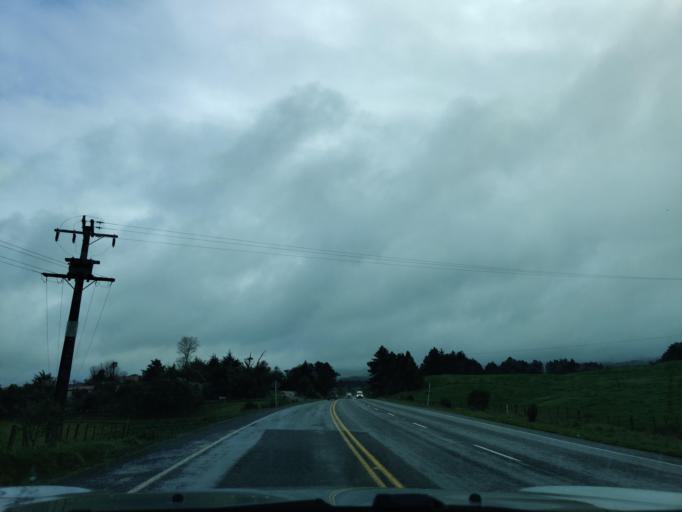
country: NZ
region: Manawatu-Wanganui
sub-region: Palmerston North City
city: Palmerston North
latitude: -40.0817
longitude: 176.2029
